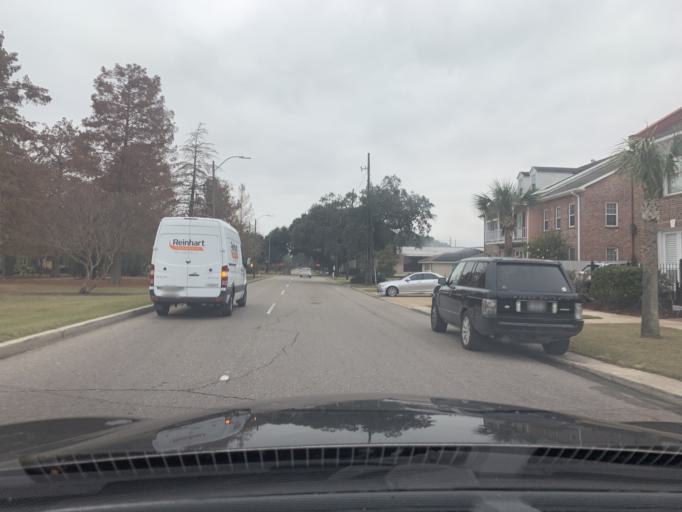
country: US
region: Louisiana
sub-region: Jefferson Parish
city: Metairie
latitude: 30.0194
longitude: -90.1065
